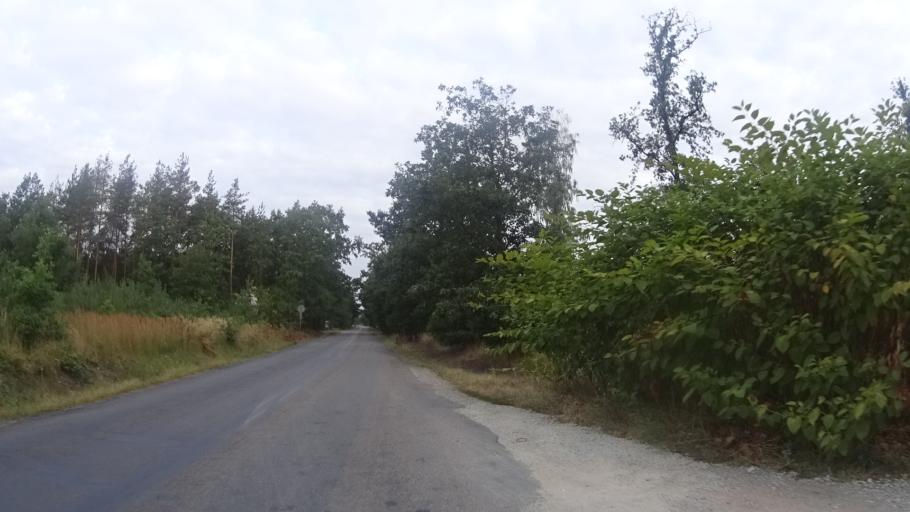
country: CZ
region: Kralovehradecky
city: Cernilov
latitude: 50.2051
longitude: 15.9274
